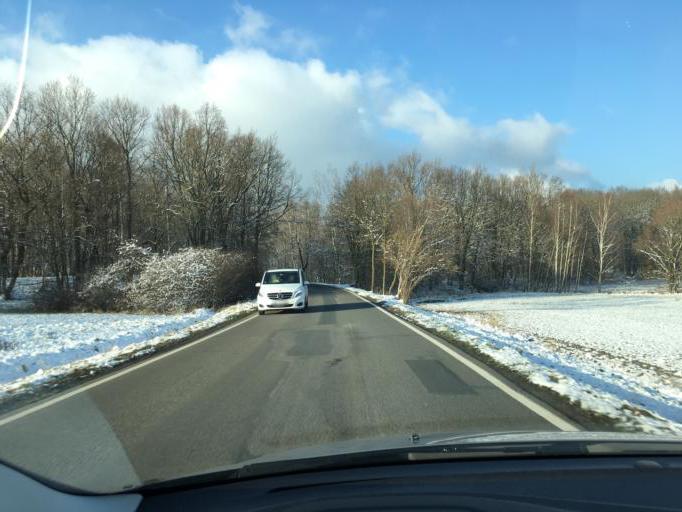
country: DE
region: Saxony
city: Grimma
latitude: 51.2668
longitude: 12.6705
